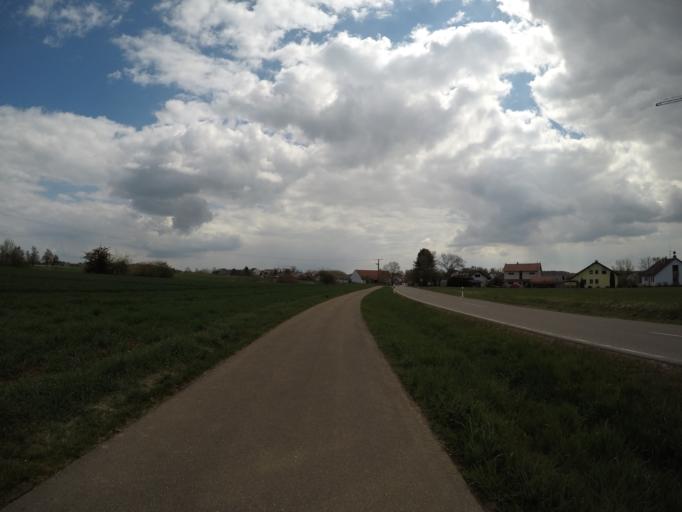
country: DE
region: Baden-Wuerttemberg
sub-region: Tuebingen Region
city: Dornstadt
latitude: 48.4465
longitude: 9.8878
